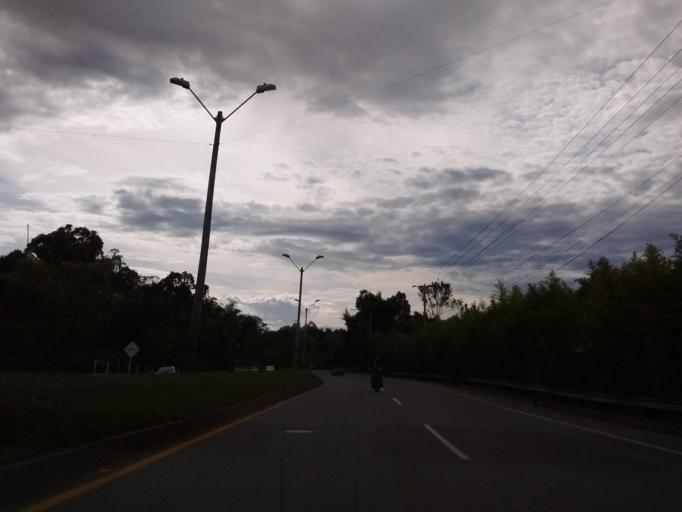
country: CO
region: Antioquia
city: Santuario
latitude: 6.1368
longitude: -75.2793
